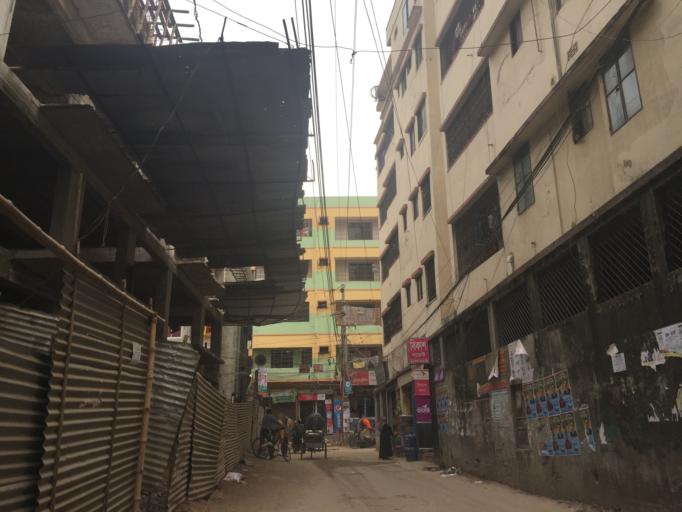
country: BD
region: Dhaka
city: Azimpur
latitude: 23.7785
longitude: 90.3654
